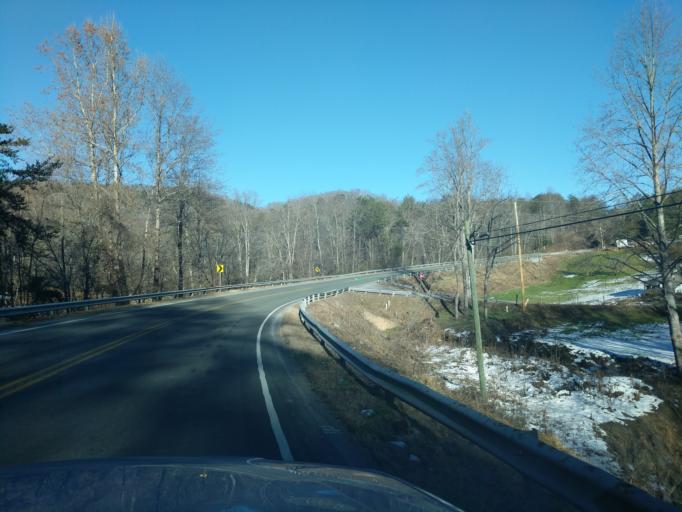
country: US
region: Georgia
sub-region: Towns County
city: Hiawassee
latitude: 34.9241
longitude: -83.6908
